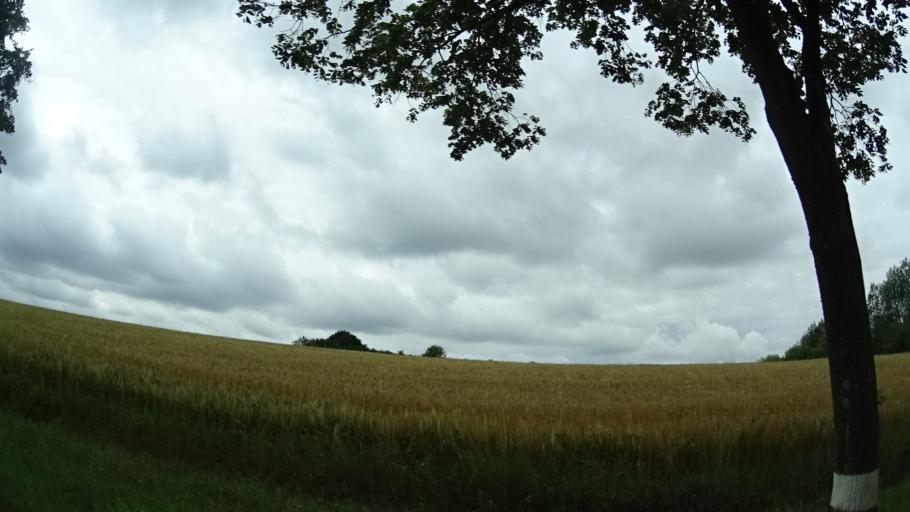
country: LU
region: Grevenmacher
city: Schengen
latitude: 49.4702
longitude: 6.3379
